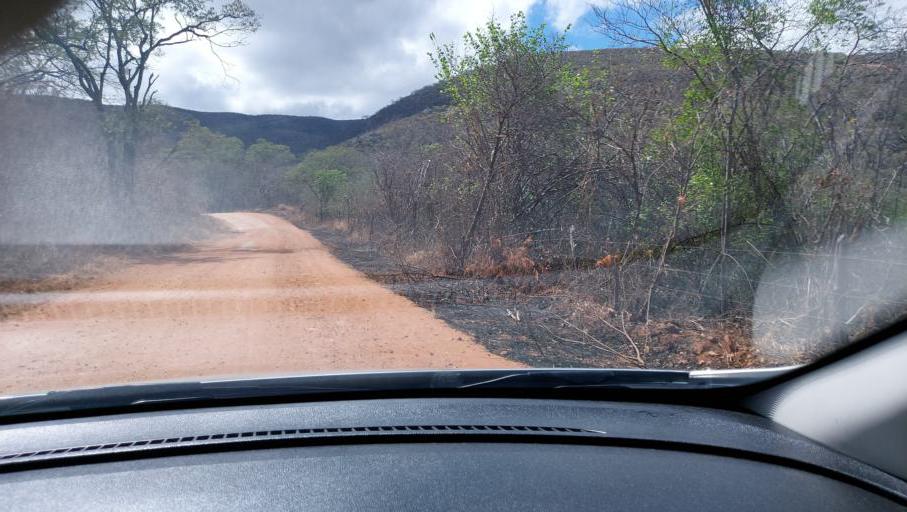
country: BR
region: Bahia
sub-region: Oliveira Dos Brejinhos
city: Beira Rio
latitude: -12.0979
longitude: -42.5503
